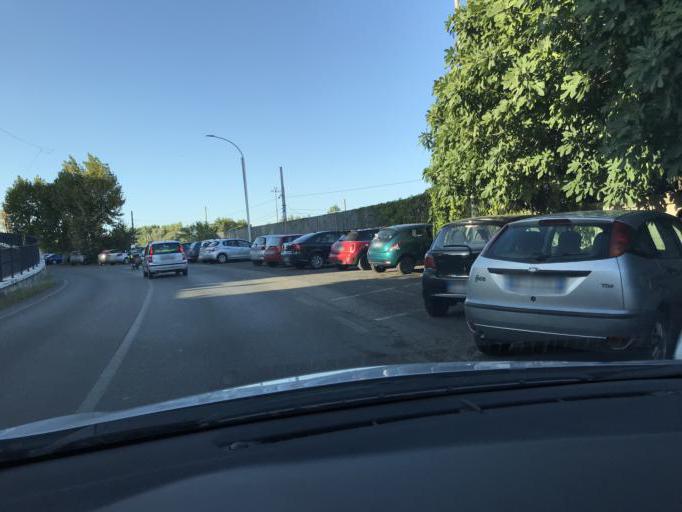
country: IT
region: Latium
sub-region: Provincia di Viterbo
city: Orte Scalo
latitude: 42.4405
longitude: 12.4079
